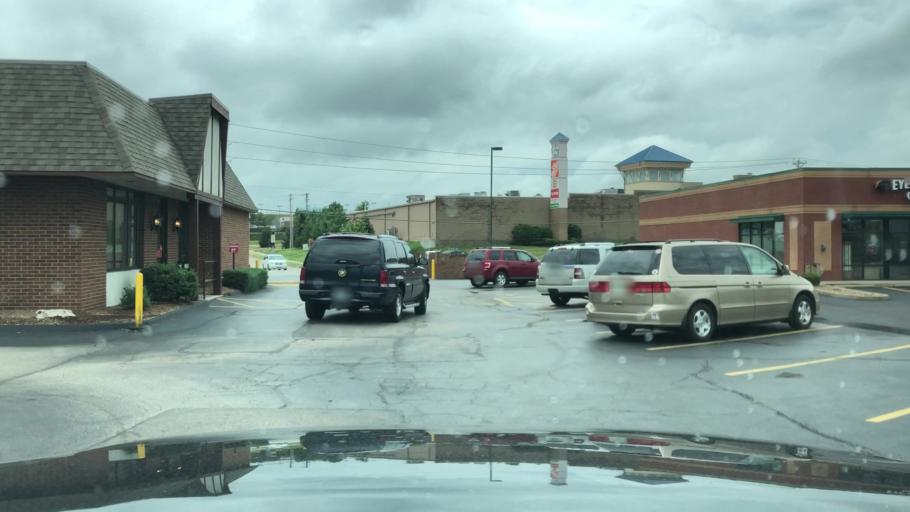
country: US
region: Missouri
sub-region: Saint Charles County
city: Saint Peters
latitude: 38.7917
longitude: -90.5613
